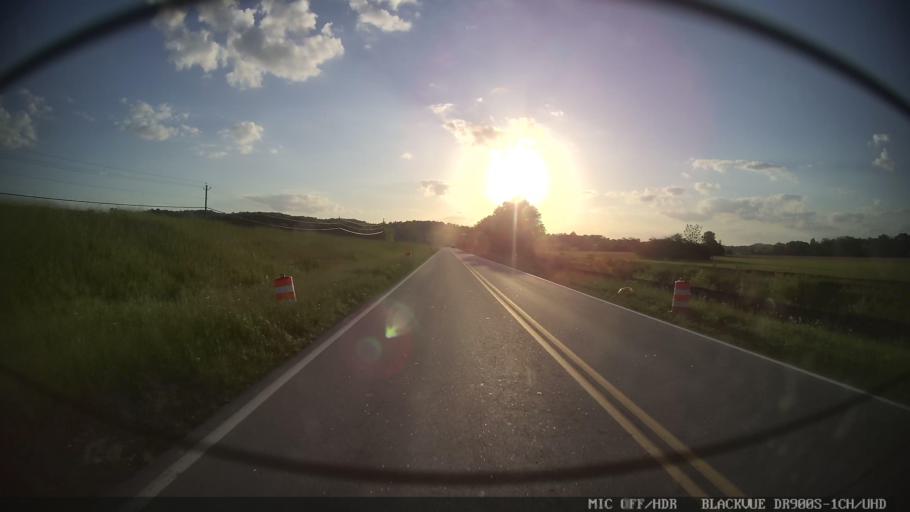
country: US
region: Georgia
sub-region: Bartow County
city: Emerson
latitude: 34.1154
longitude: -84.7847
